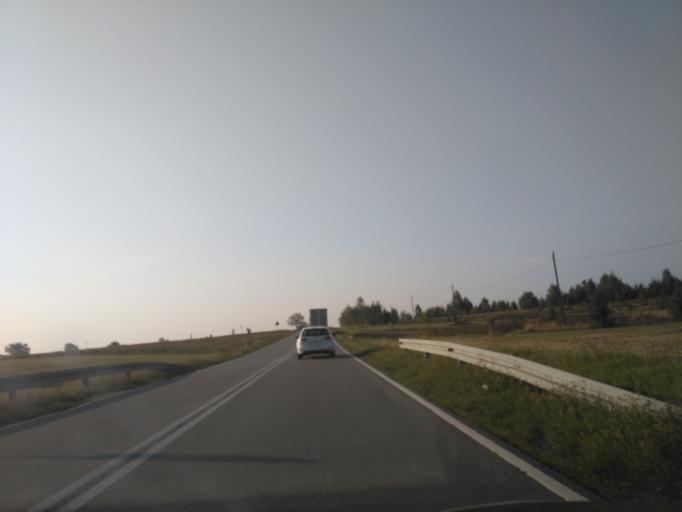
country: PL
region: Lublin Voivodeship
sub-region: Powiat janowski
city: Modliborzyce
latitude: 50.7892
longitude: 22.3184
